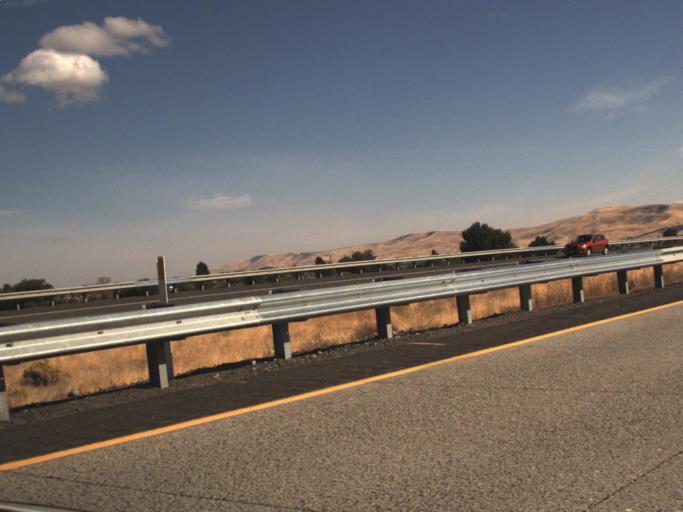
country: US
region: Washington
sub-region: Benton County
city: Prosser
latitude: 46.2372
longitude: -119.8166
